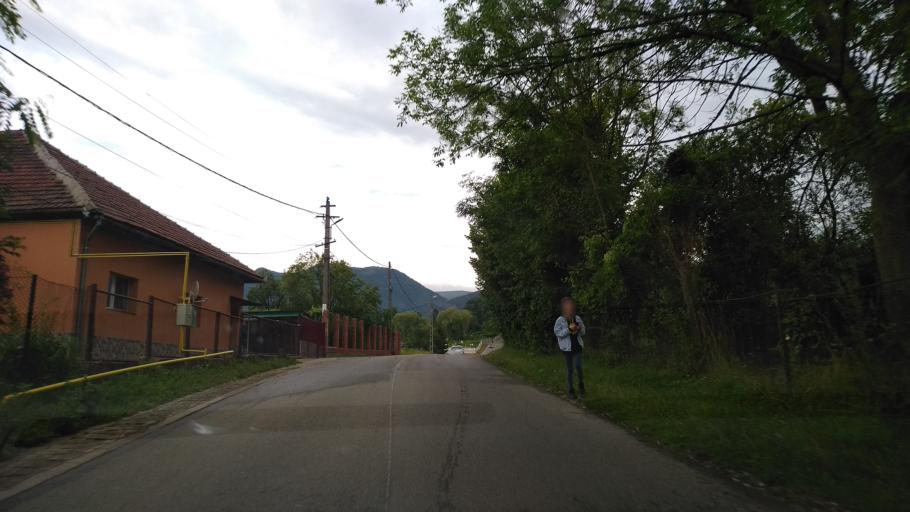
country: RO
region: Hunedoara
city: Vulcan
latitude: 45.3711
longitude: 23.2816
